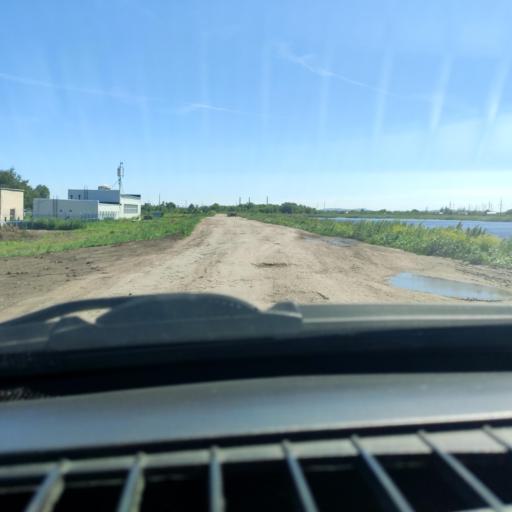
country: RU
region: Samara
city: Tol'yatti
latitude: 53.5936
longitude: 49.4384
